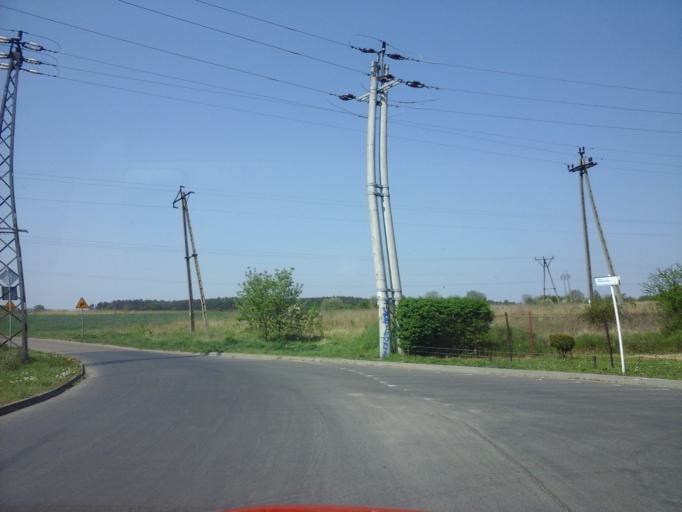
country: PL
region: West Pomeranian Voivodeship
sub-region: Powiat choszczenski
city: Choszczno
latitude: 53.1642
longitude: 15.3955
